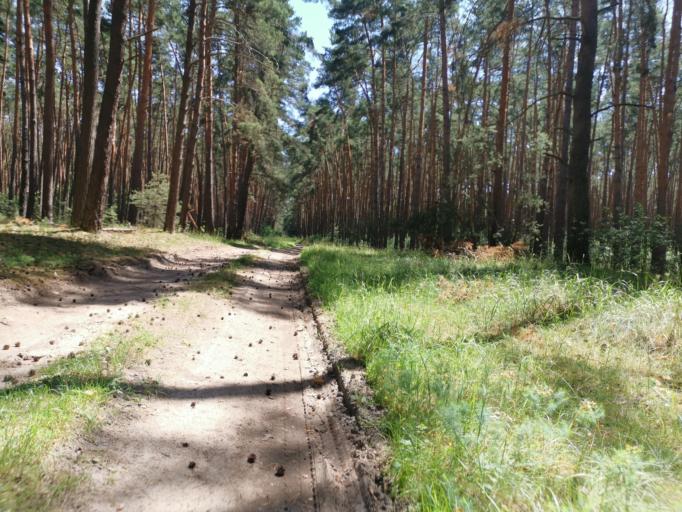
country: CZ
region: South Moravian
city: Vracov
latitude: 48.9607
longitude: 17.2226
